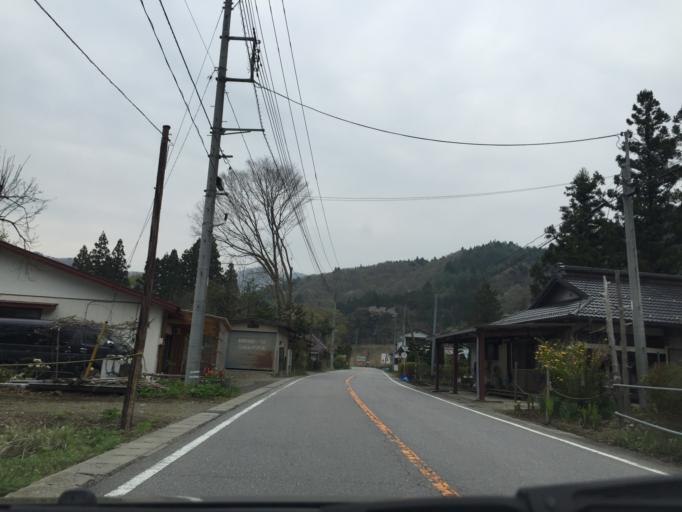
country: JP
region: Tochigi
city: Nikko
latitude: 36.9766
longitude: 139.6907
